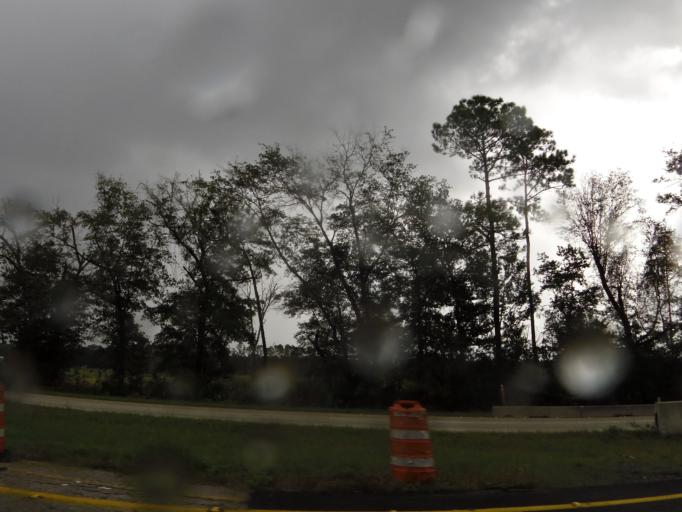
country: US
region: Florida
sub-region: Bradford County
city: Starke
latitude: 30.0006
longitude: -82.0925
